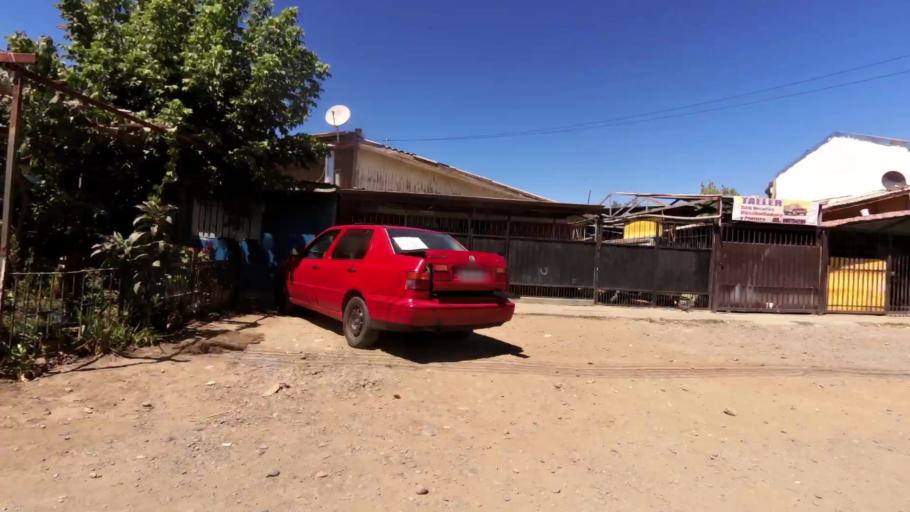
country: CL
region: O'Higgins
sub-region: Provincia de Cachapoal
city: Rancagua
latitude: -34.1613
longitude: -70.7215
